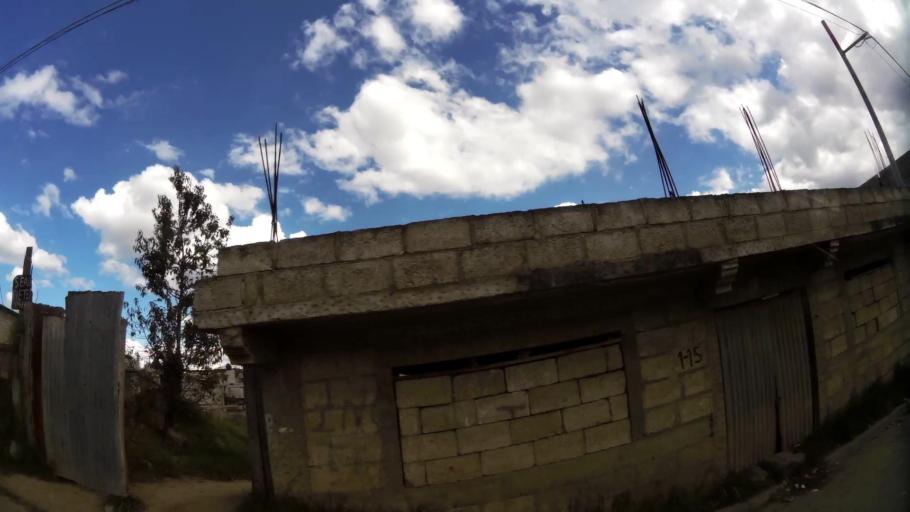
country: GT
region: Quetzaltenango
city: Quetzaltenango
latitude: 14.8382
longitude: -91.5422
